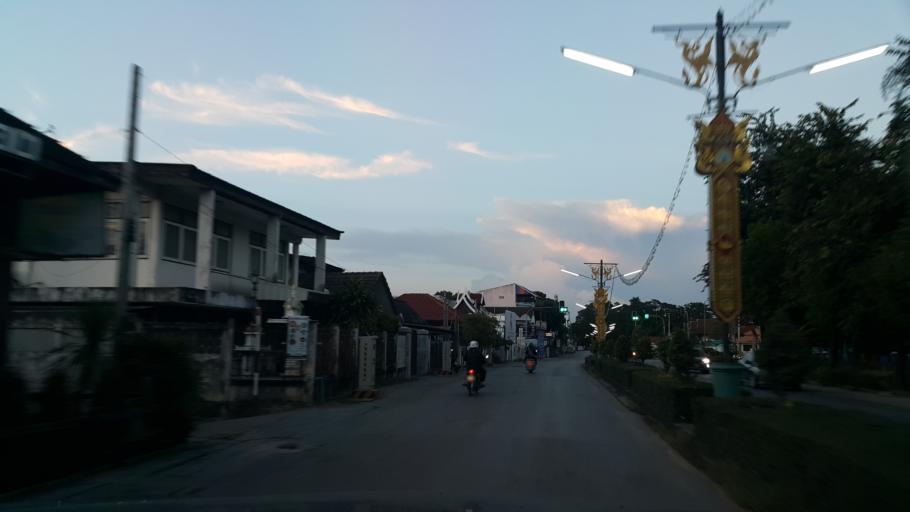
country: TH
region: Lamphun
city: Lamphun
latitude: 18.5735
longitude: 99.0084
